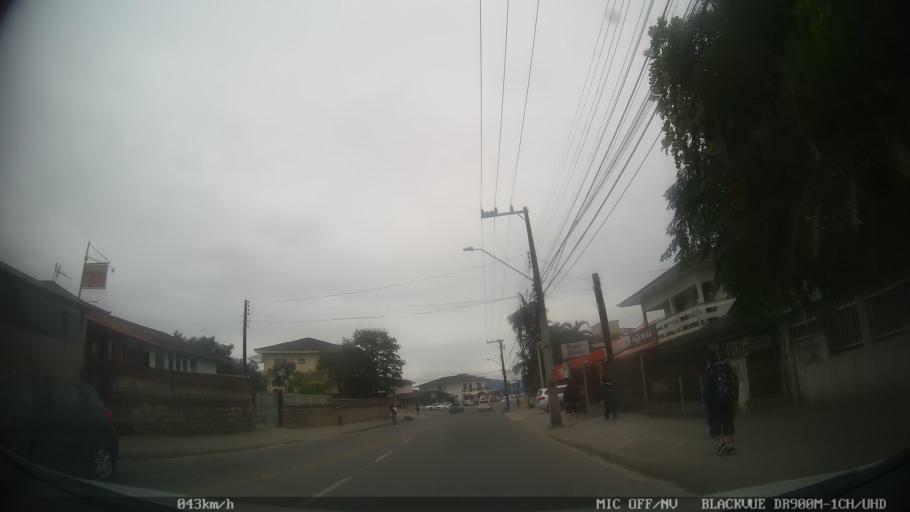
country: BR
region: Santa Catarina
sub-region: Joinville
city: Joinville
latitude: -26.3380
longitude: -48.8170
